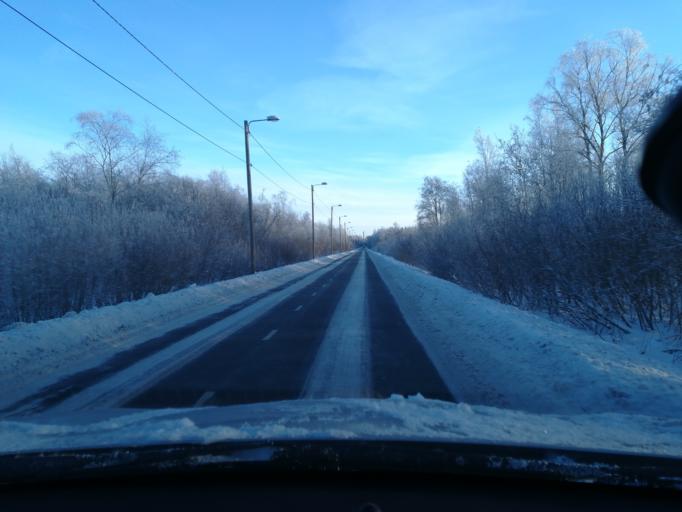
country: EE
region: Harju
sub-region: Saue vald
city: Laagri
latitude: 59.3938
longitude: 24.6004
